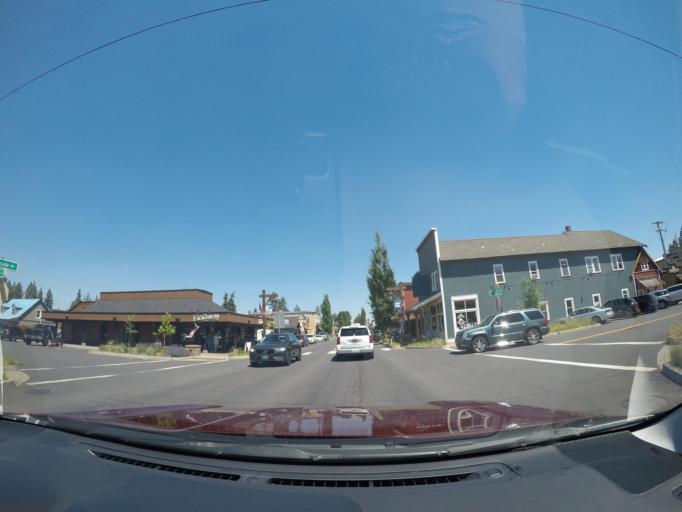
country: US
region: Oregon
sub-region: Deschutes County
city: Sisters
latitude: 44.2913
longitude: -121.5501
